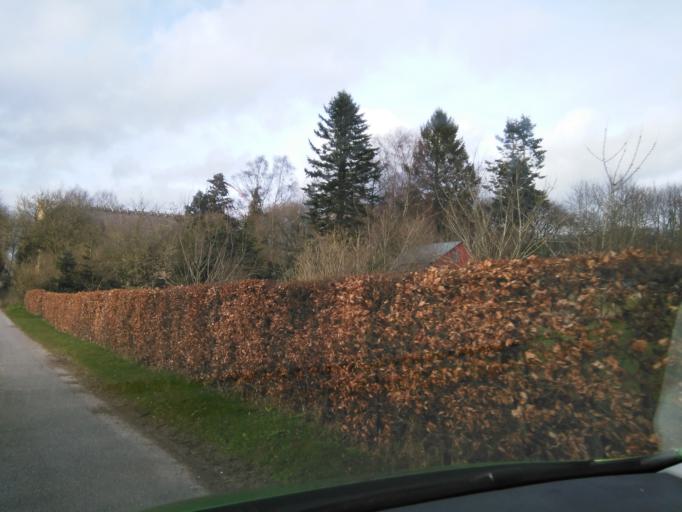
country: DK
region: Central Jutland
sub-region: Arhus Kommune
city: Trige
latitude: 56.2078
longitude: 10.1315
